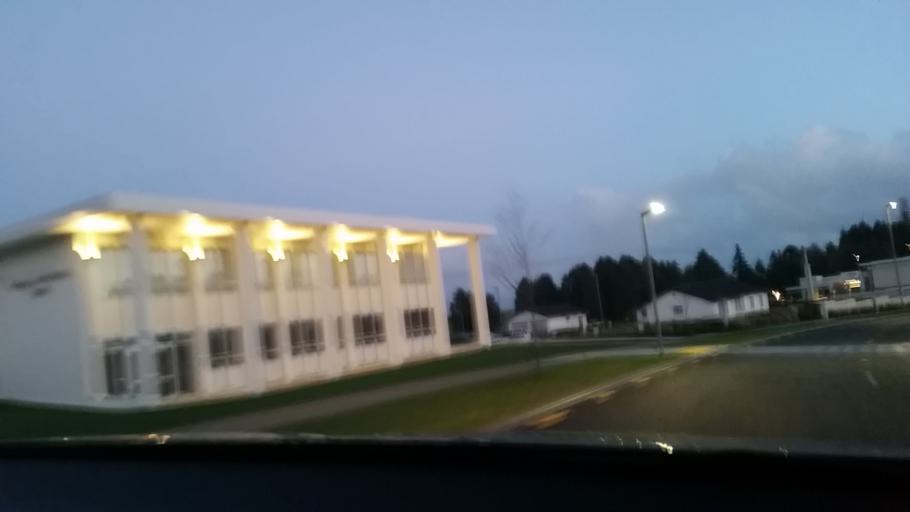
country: NZ
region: Waikato
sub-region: Hamilton City
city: Hamilton
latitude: -37.8207
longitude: 175.2268
